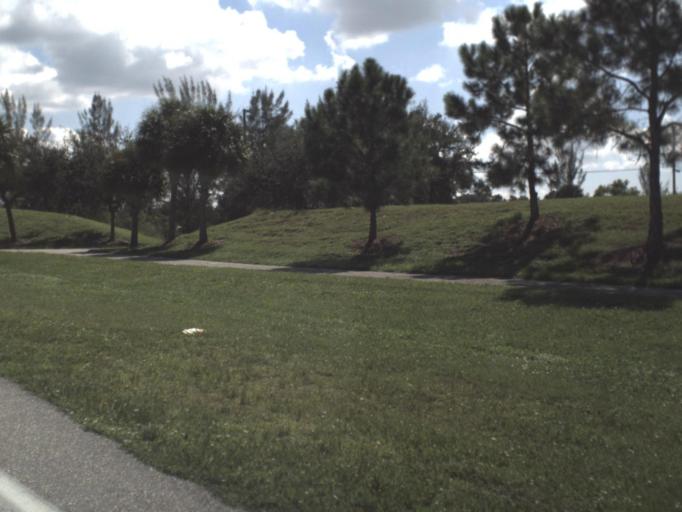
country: US
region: Florida
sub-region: Lee County
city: Cape Coral
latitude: 26.6070
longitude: -81.9975
